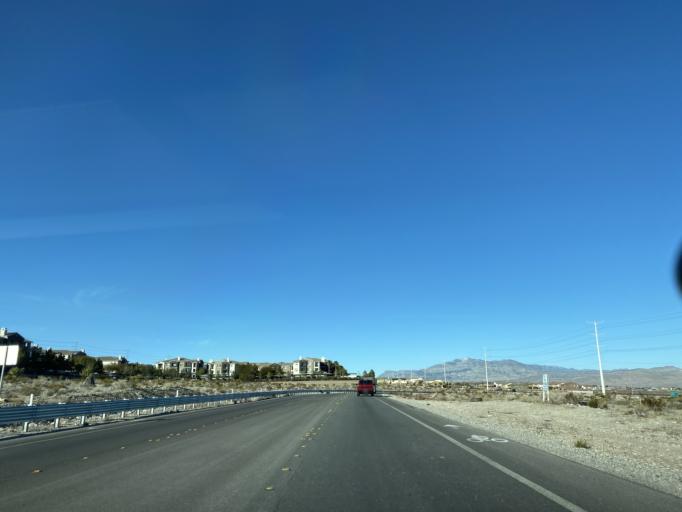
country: US
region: Nevada
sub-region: Clark County
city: Summerlin South
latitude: 36.2729
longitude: -115.3301
